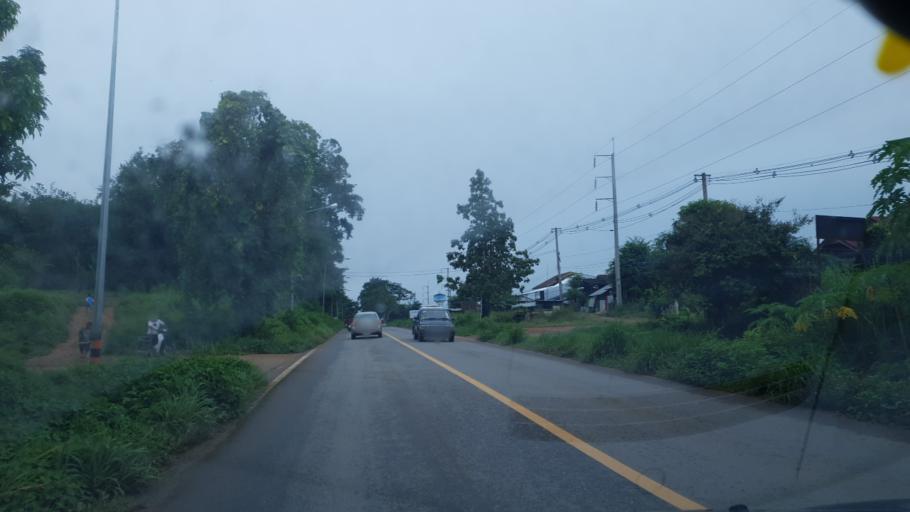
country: TH
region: Mae Hong Son
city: Ban Huai I Huak
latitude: 18.1753
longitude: 97.9341
